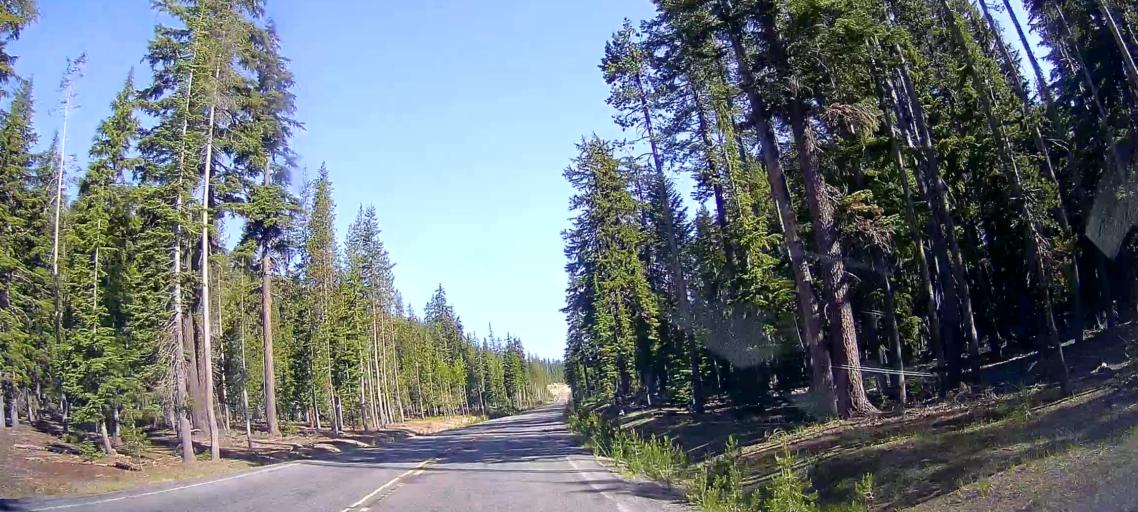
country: US
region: Oregon
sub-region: Jackson County
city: Shady Cove
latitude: 42.8612
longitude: -122.1657
